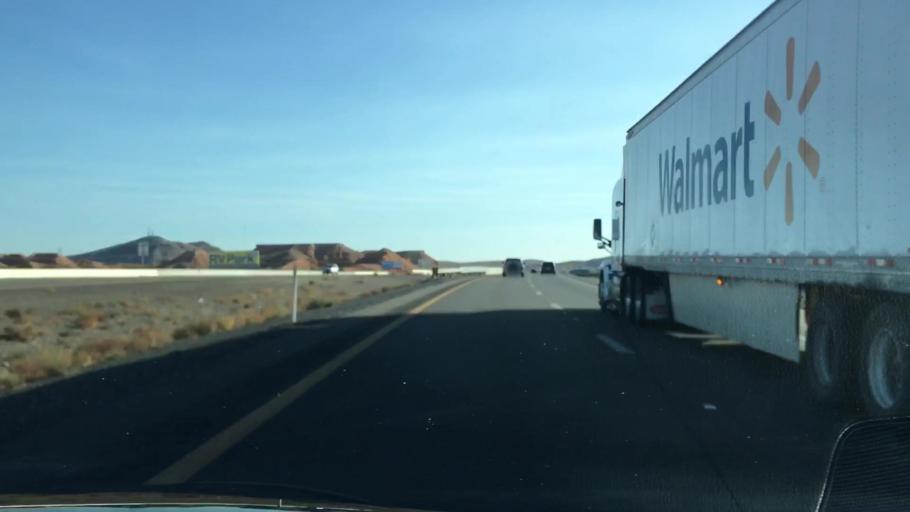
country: US
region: Nevada
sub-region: Clark County
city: Moapa Town
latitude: 36.6650
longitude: -114.5640
